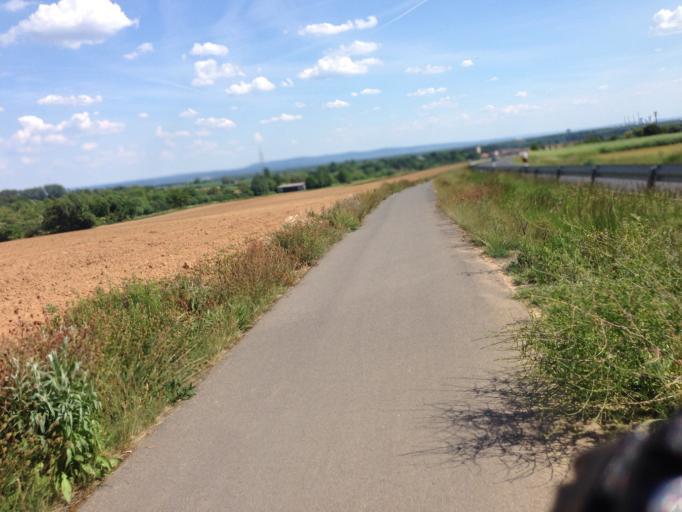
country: DE
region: Hesse
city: Bruchkobel
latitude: 50.1907
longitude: 8.8788
